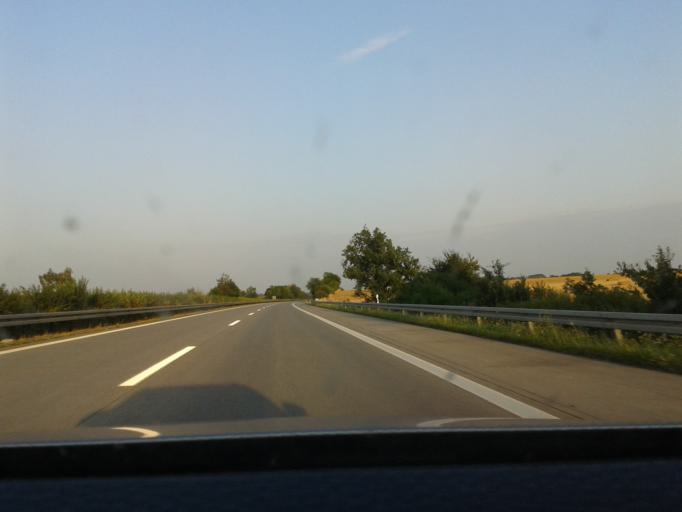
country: DE
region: Saxony
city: Mochau
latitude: 51.1047
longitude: 13.1954
